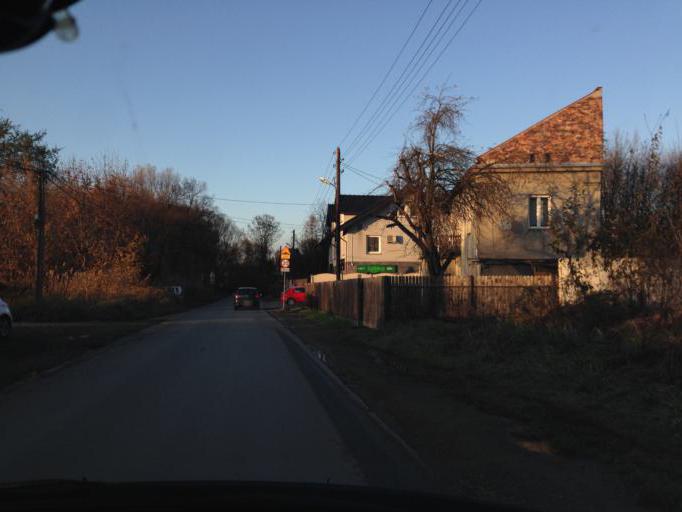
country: PL
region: Lesser Poland Voivodeship
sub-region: Powiat krakowski
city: Rzaska
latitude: 50.0728
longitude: 19.8777
